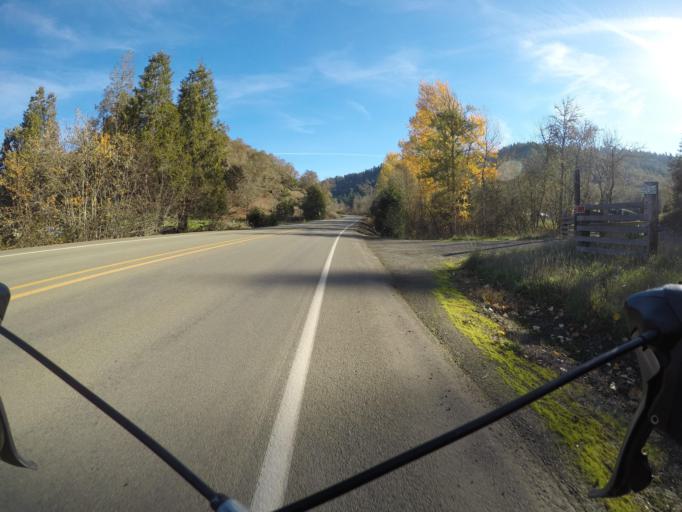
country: US
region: Oregon
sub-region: Douglas County
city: Winston
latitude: 43.1877
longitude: -123.4547
